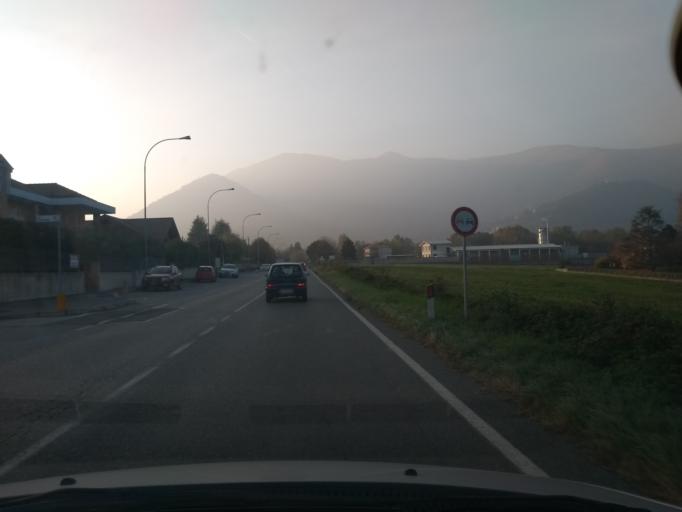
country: IT
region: Piedmont
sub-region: Provincia di Torino
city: Givoletto
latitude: 45.1523
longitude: 7.5104
